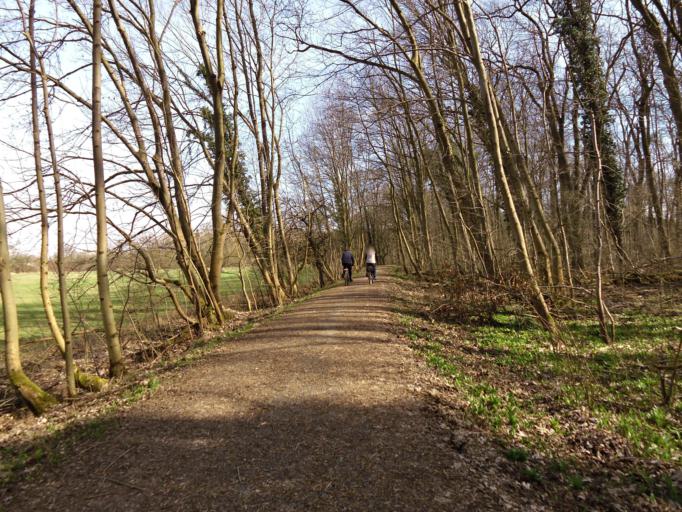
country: DE
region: Hesse
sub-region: Regierungsbezirk Darmstadt
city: Stockstadt am Rhein
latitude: 49.8304
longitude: 8.4624
